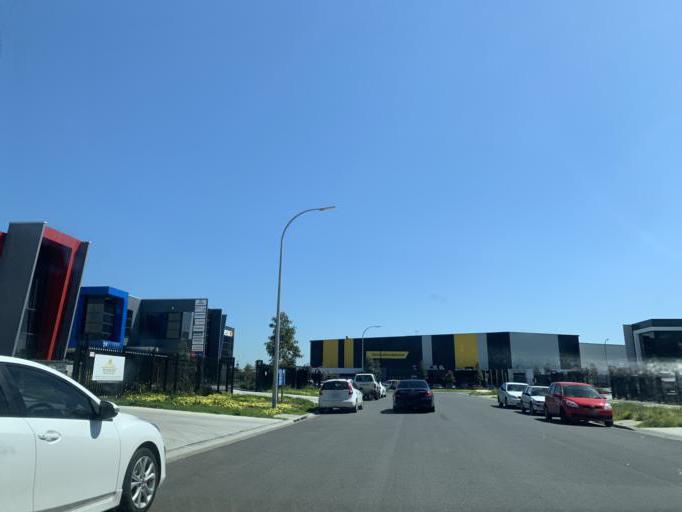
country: AU
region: Victoria
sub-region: Greater Dandenong
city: Keysborough
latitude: -38.0085
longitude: 145.1836
